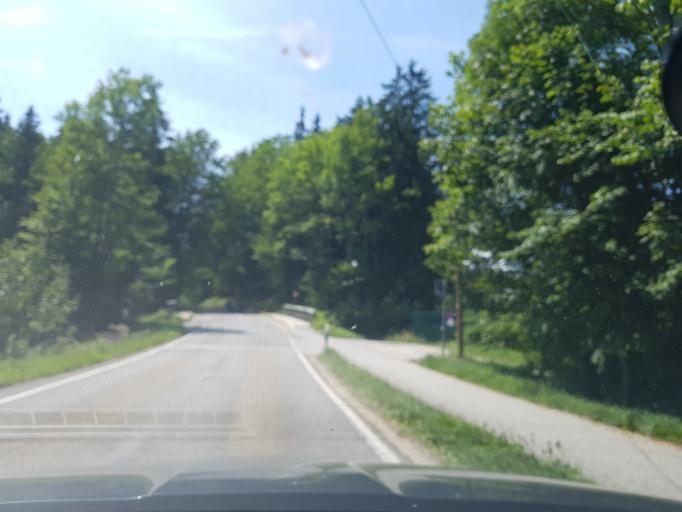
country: DE
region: Bavaria
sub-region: Upper Bavaria
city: Berchtesgaden
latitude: 47.6440
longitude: 12.9866
